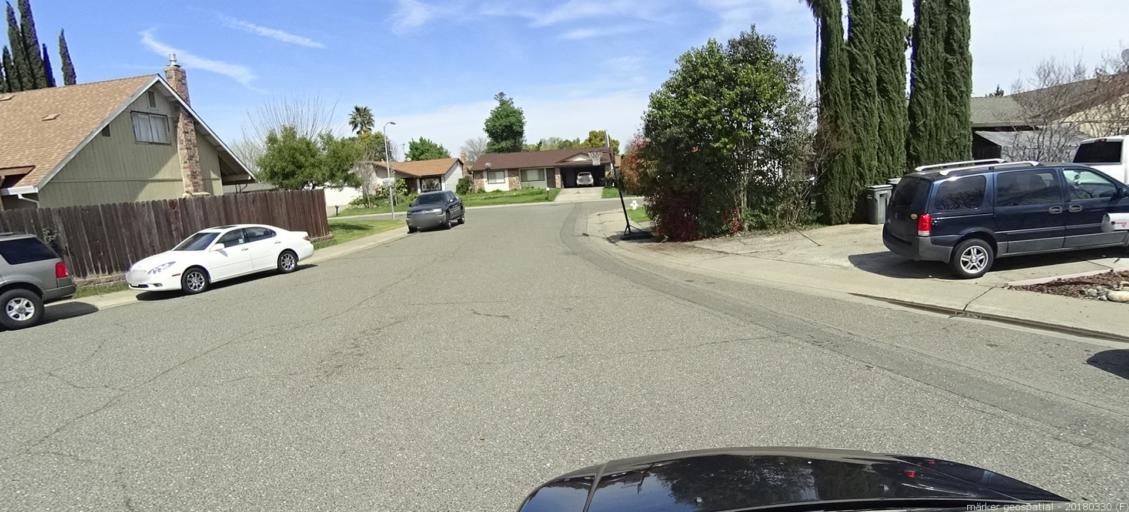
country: US
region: California
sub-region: Sacramento County
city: Rosemont
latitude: 38.5401
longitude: -121.3676
